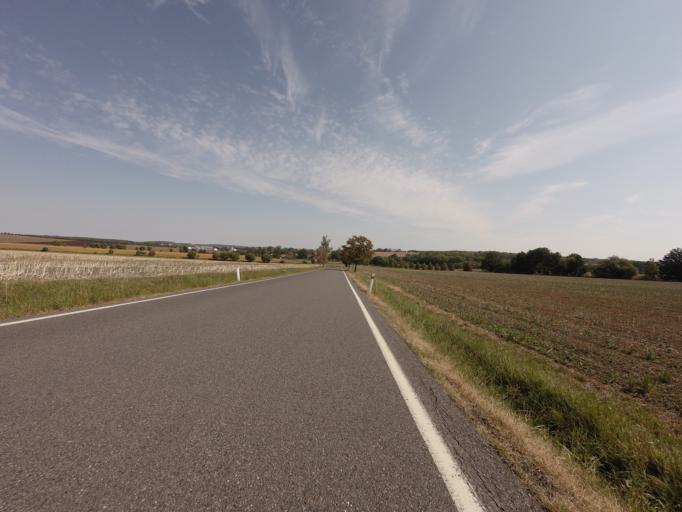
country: CZ
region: Jihocesky
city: Bernartice
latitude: 49.3530
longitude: 14.3745
